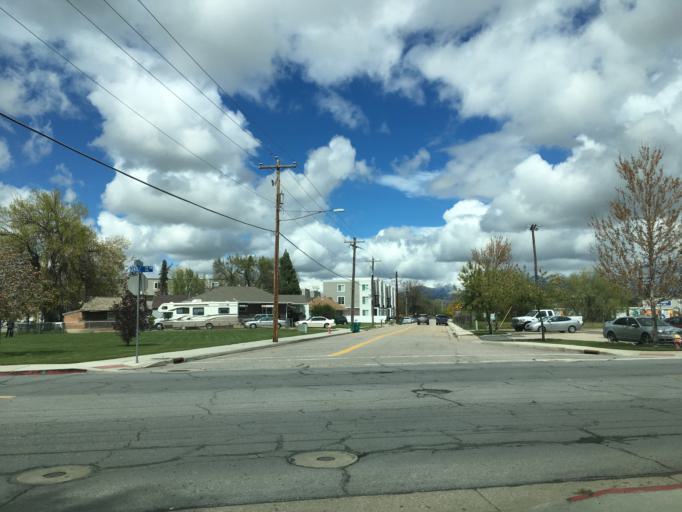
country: US
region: Utah
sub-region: Davis County
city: Layton
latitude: 41.0601
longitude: -111.9689
